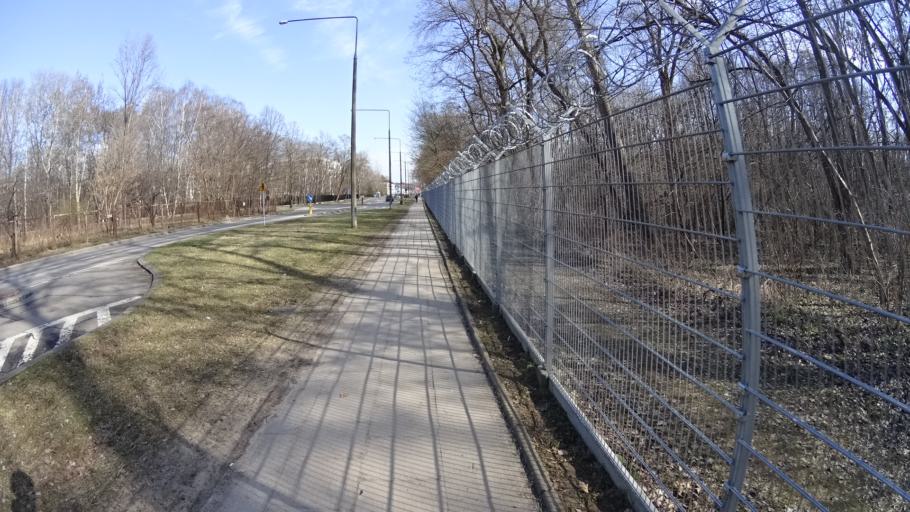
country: PL
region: Masovian Voivodeship
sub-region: Warszawa
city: Bemowo
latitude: 52.2534
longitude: 20.9313
